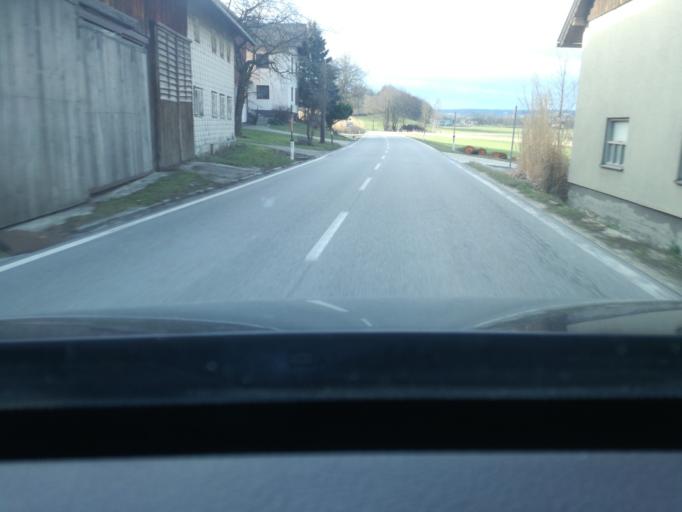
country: AT
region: Upper Austria
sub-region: Politischer Bezirk Ried im Innkreis
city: Waldzell
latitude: 48.1609
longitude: 13.4236
